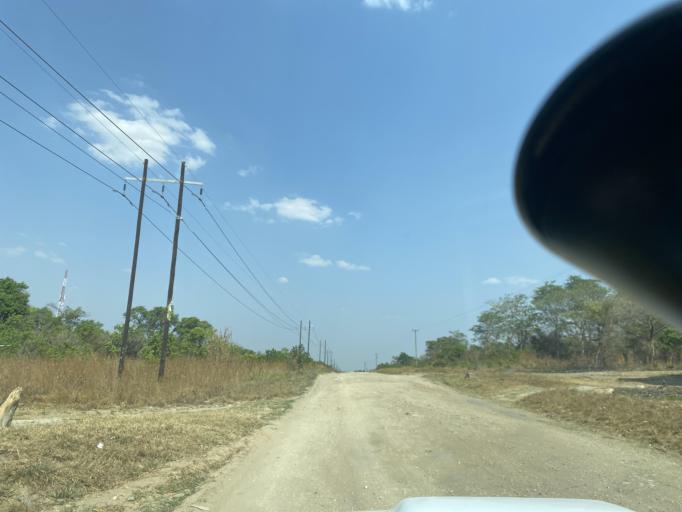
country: ZM
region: Lusaka
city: Lusaka
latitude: -15.3099
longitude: 28.0470
